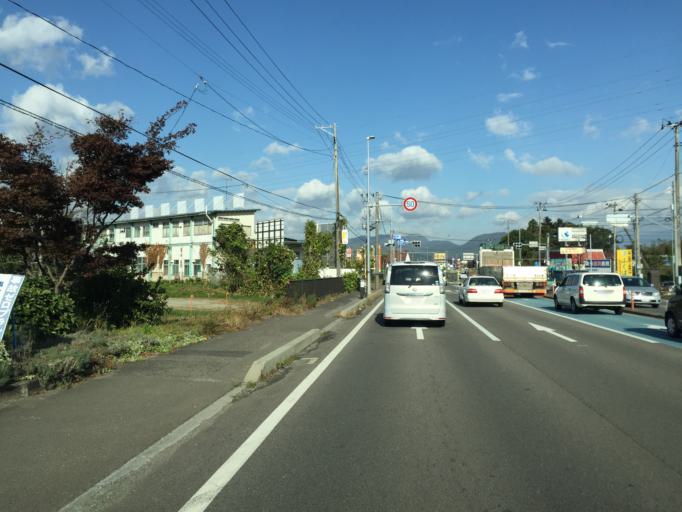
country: JP
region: Fukushima
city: Fukushima-shi
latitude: 37.7966
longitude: 140.4574
